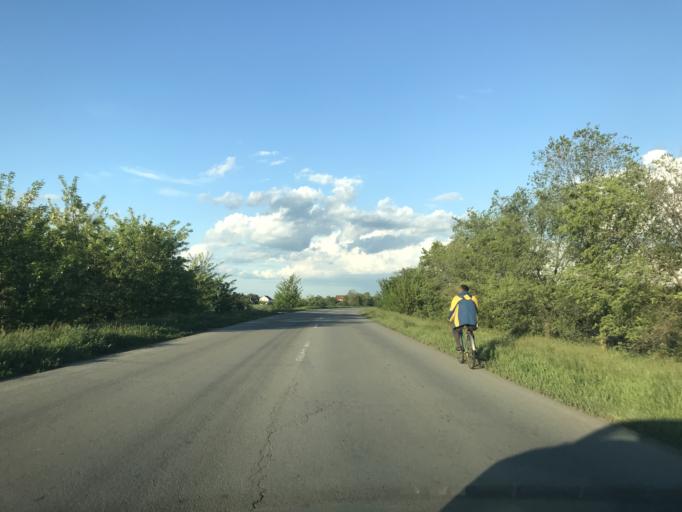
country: RS
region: Autonomna Pokrajina Vojvodina
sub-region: Srednjebanatski Okrug
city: Zrenjanin
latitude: 45.4009
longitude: 20.3684
